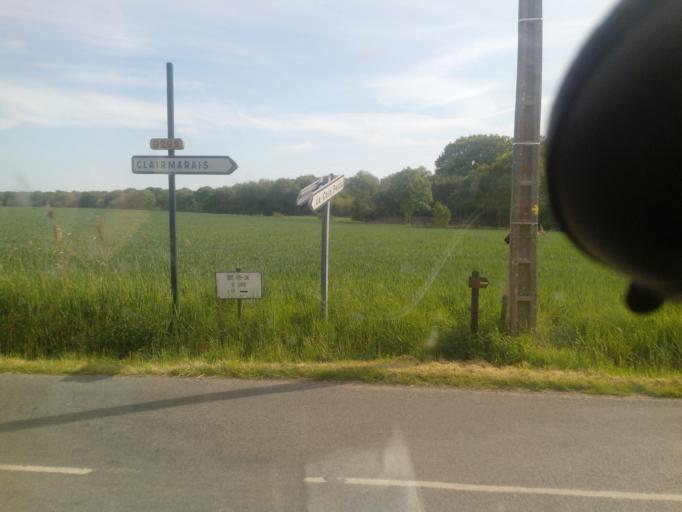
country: FR
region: Nord-Pas-de-Calais
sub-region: Departement du Nord
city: Renescure
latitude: 50.7724
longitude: 2.3586
